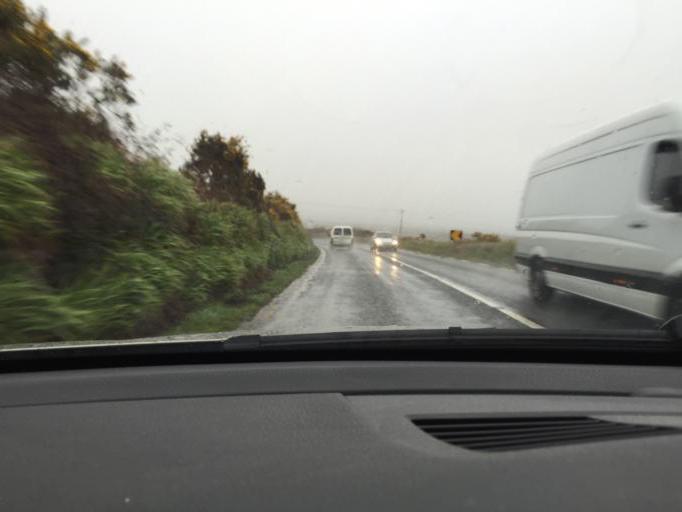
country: IE
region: Munster
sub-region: Ciarrai
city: Dingle
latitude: 52.1380
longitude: -10.2356
